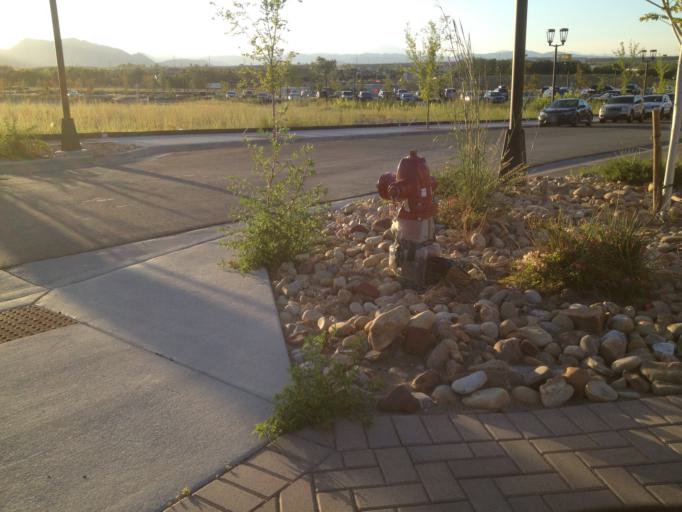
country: US
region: Colorado
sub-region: Boulder County
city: Superior
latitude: 39.9513
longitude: -105.1594
